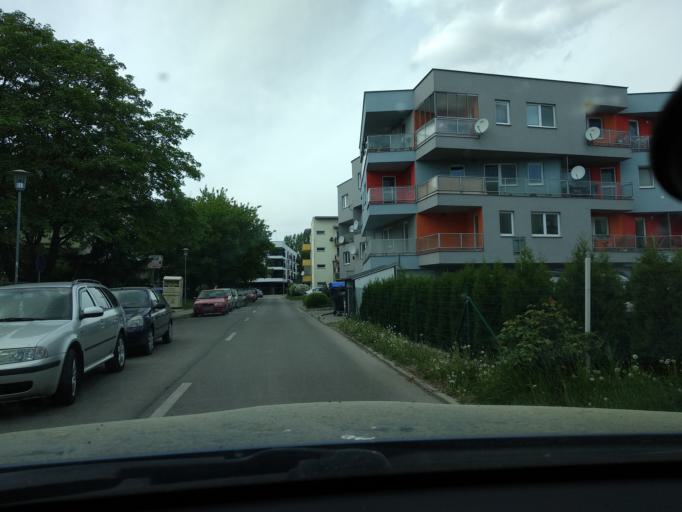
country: SK
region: Trenciansky
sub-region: Okres Trencin
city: Trencin
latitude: 48.8835
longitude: 18.0251
